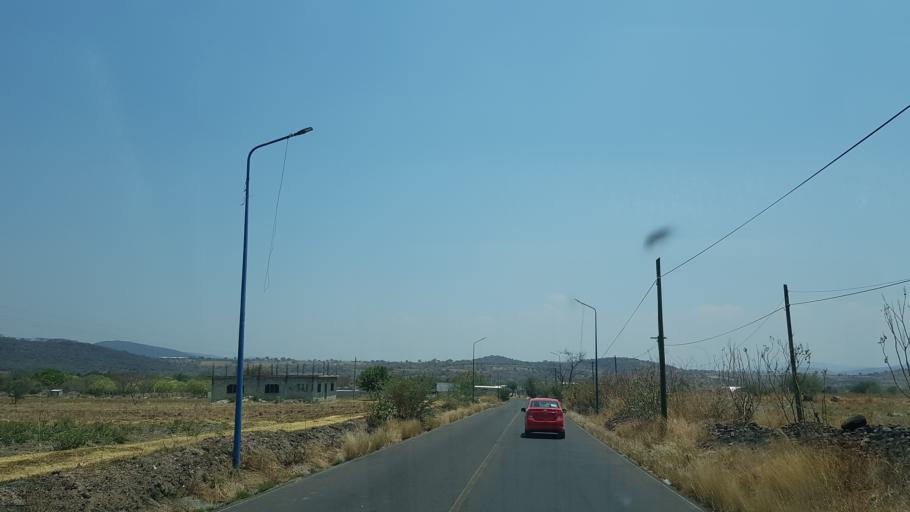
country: MX
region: Puebla
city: Huaquechula
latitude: 18.7651
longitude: -98.5304
